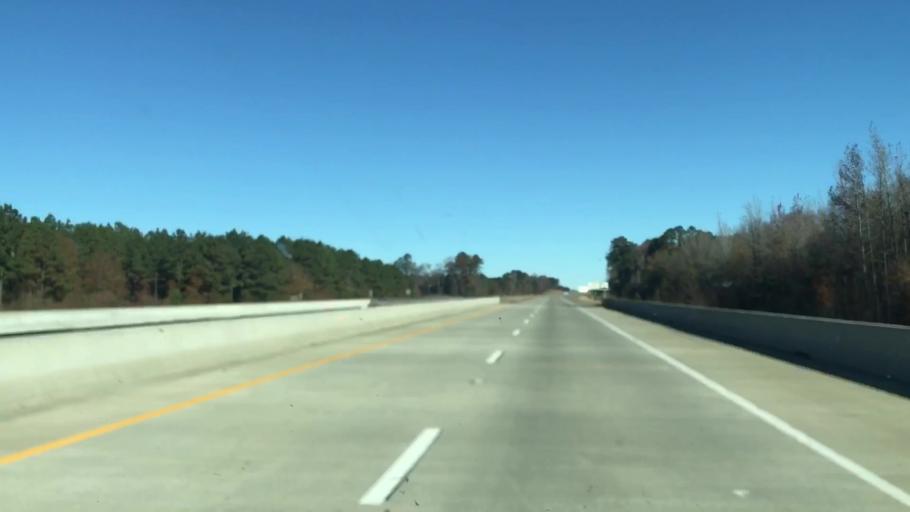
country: US
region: Louisiana
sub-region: Caddo Parish
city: Vivian
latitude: 33.0280
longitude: -93.9005
